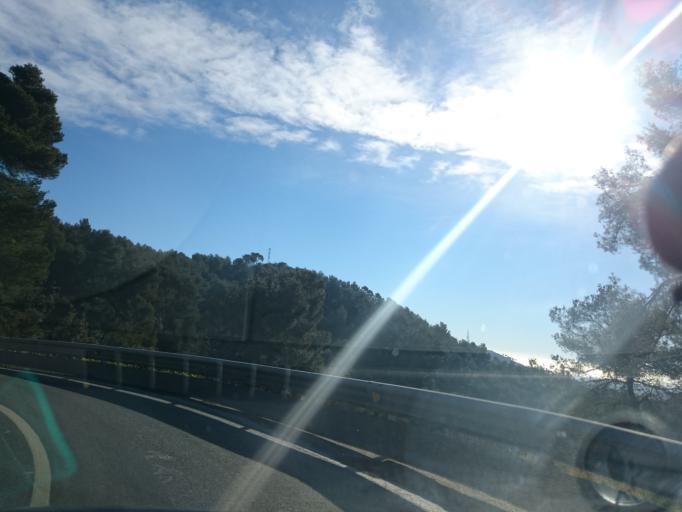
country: ES
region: Catalonia
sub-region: Provincia de Barcelona
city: Sant Just Desvern
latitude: 41.4110
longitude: 2.0808
